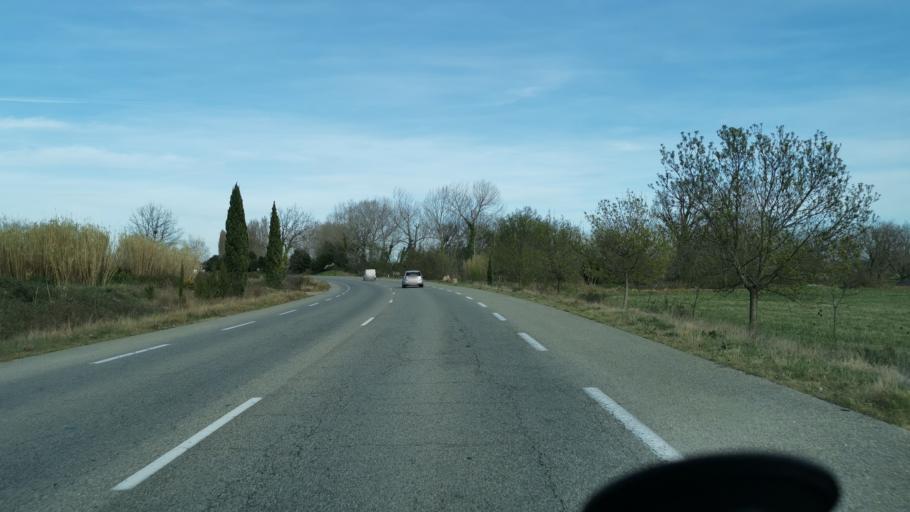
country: FR
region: Provence-Alpes-Cote d'Azur
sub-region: Departement des Bouches-du-Rhone
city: Saint-Martin-de-Crau
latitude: 43.5987
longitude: 4.7781
